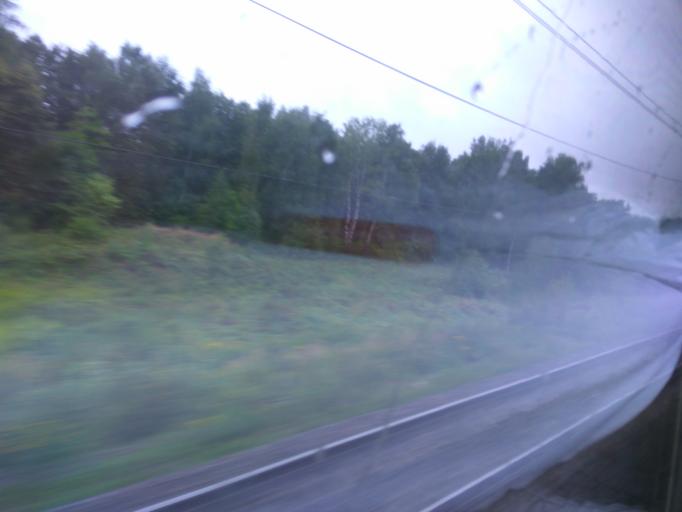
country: RU
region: Moskovskaya
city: Kashira
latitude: 54.8479
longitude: 38.2262
